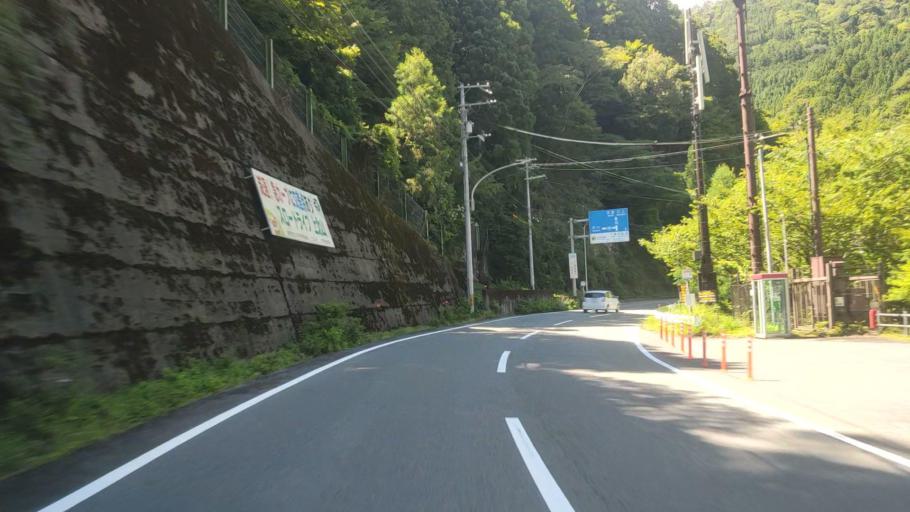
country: JP
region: Mie
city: Owase
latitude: 34.1908
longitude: 135.9936
